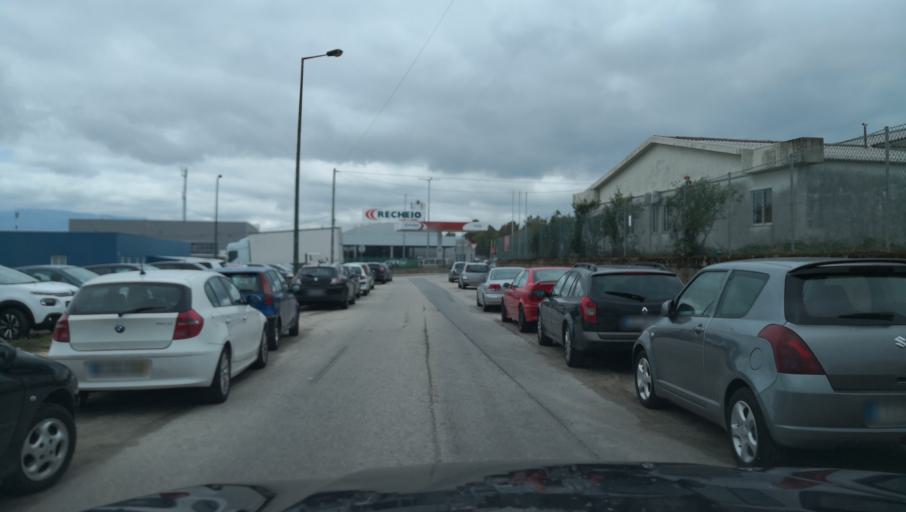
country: PT
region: Vila Real
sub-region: Vila Real
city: Vila Real
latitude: 41.2750
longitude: -7.7049
